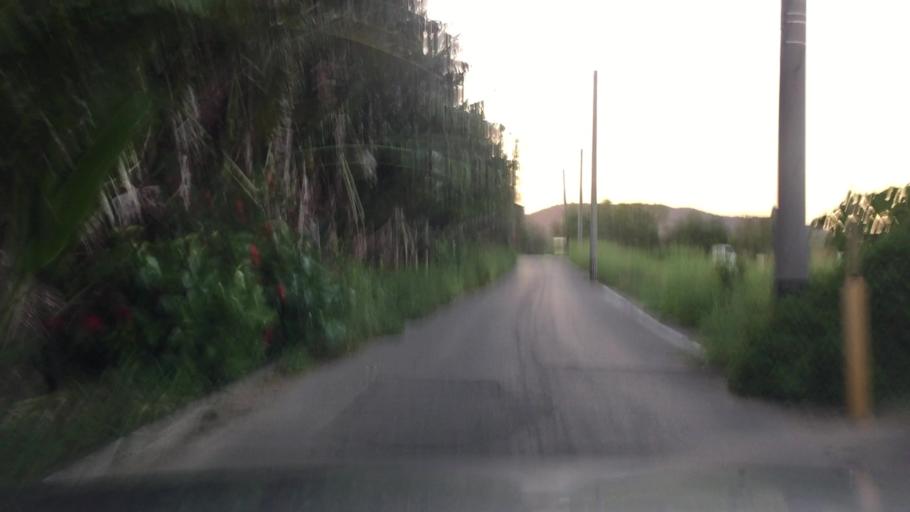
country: JP
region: Okinawa
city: Ishigaki
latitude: 24.3527
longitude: 124.1640
